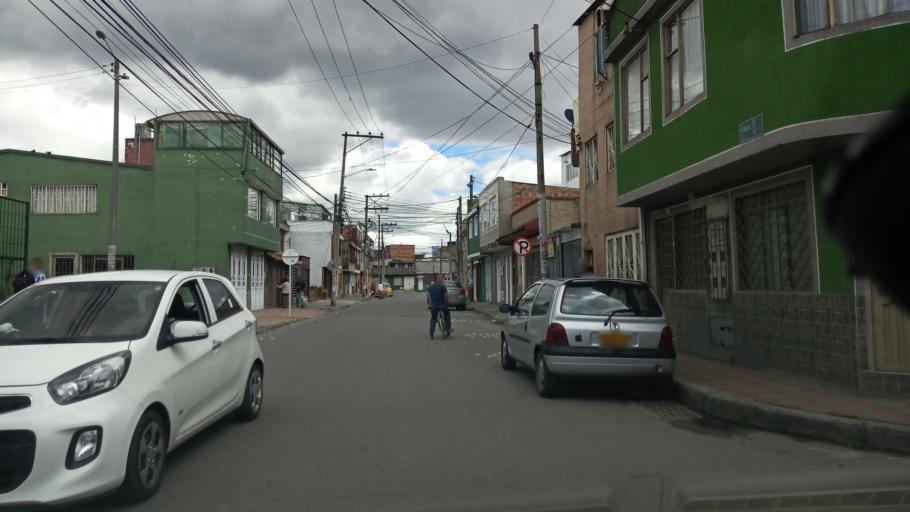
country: CO
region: Cundinamarca
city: Funza
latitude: 4.6693
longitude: -74.1472
